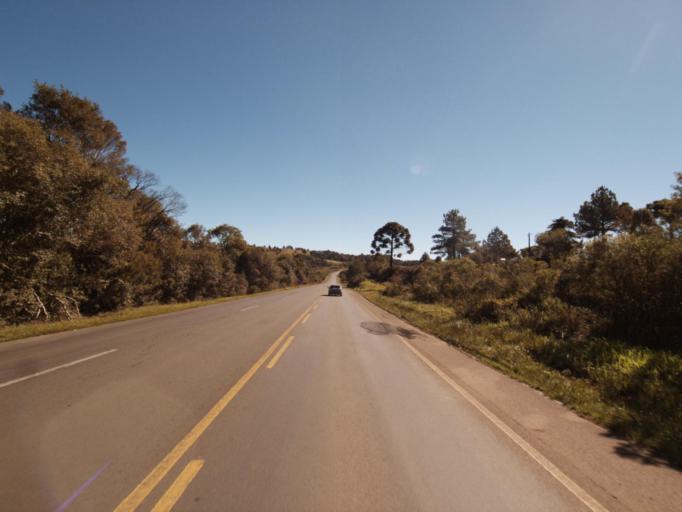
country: BR
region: Santa Catarina
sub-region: Concordia
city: Concordia
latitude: -26.9121
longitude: -51.9635
